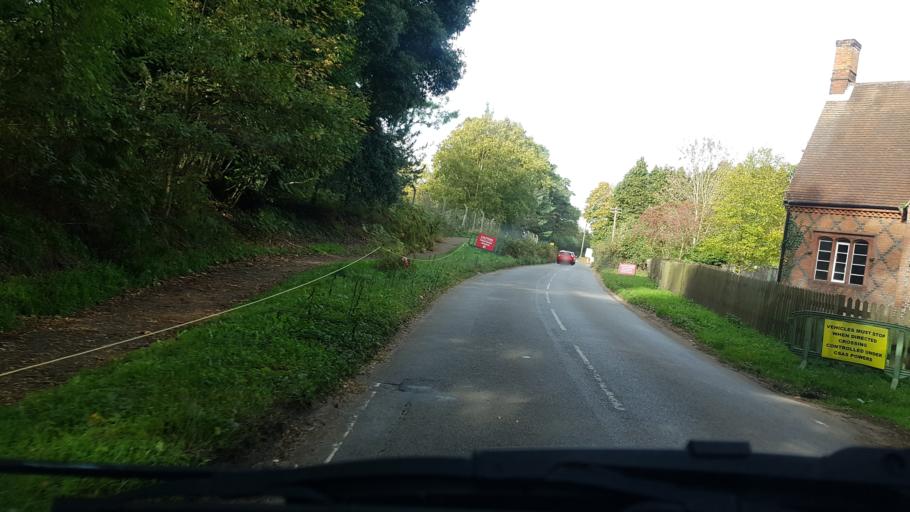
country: GB
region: England
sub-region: Surrey
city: Byfleet
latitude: 51.3203
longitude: -0.4737
